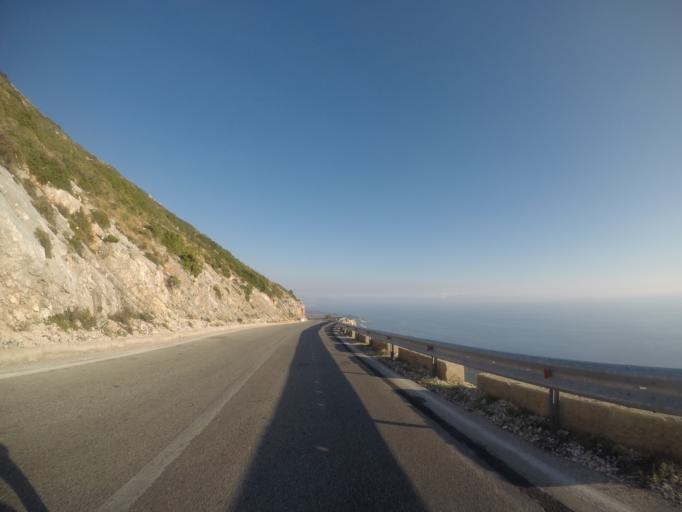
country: AL
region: Vlore
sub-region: Rrethi i Vlores
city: Vranisht
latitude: 40.1839
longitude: 19.5961
